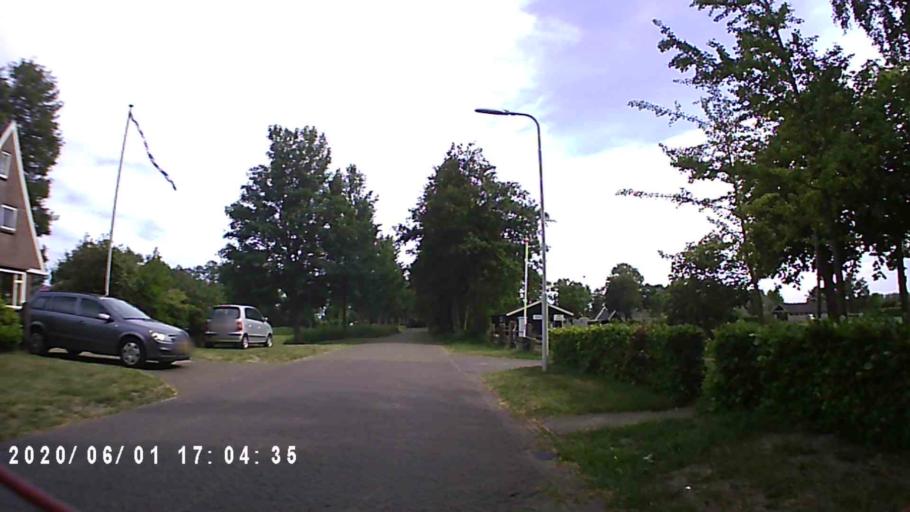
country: NL
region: Friesland
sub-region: Gemeente Tytsjerksteradiel
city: Garyp
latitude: 53.1738
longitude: 5.9335
